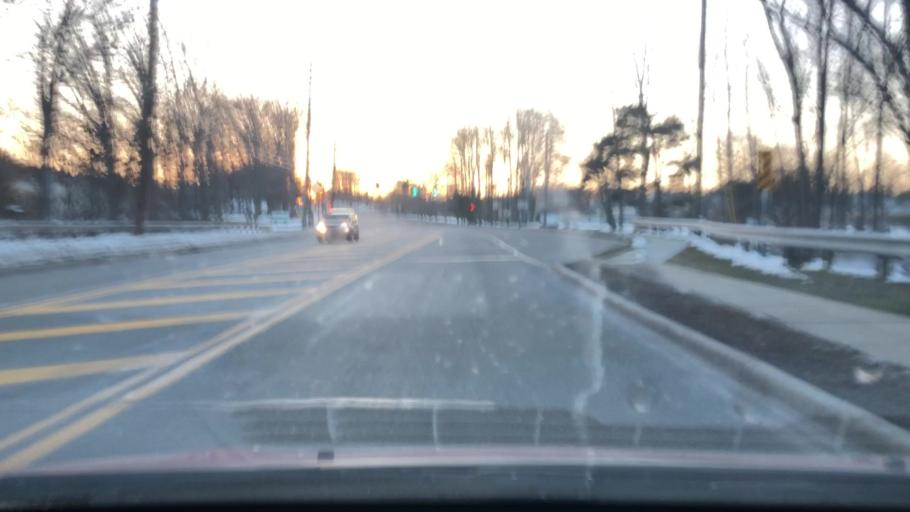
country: US
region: Ohio
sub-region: Cuyahoga County
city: Independence
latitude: 41.3619
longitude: -81.6227
